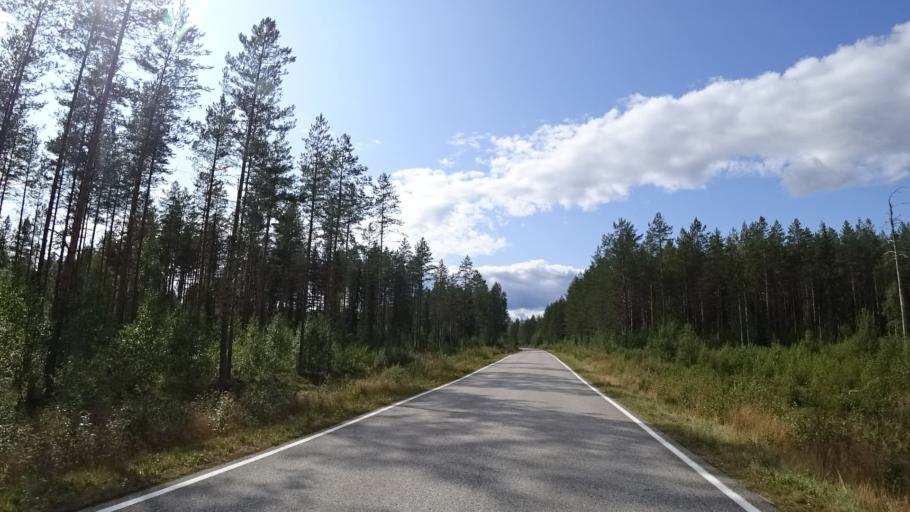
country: FI
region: North Karelia
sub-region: Joensuu
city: Ilomantsi
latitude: 62.4126
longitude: 30.9902
